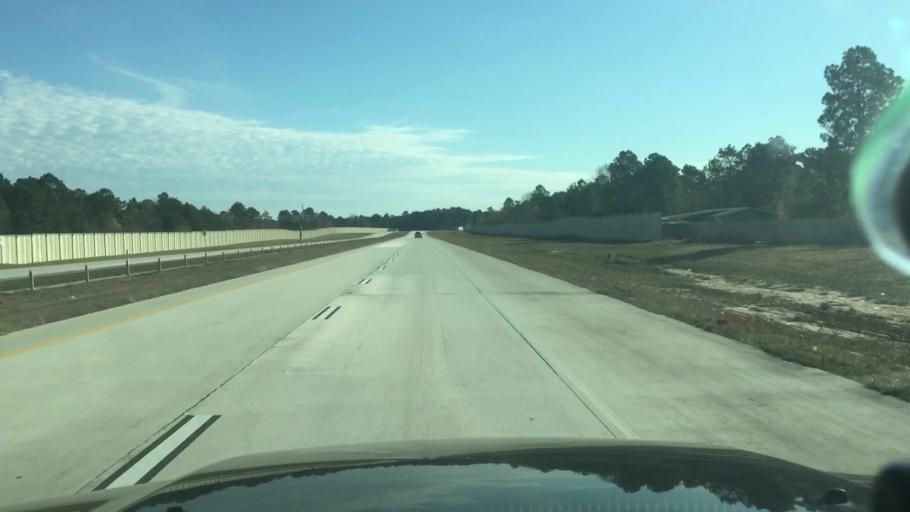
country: US
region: Texas
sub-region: Montgomery County
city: Porter Heights
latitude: 30.1377
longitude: -95.2674
